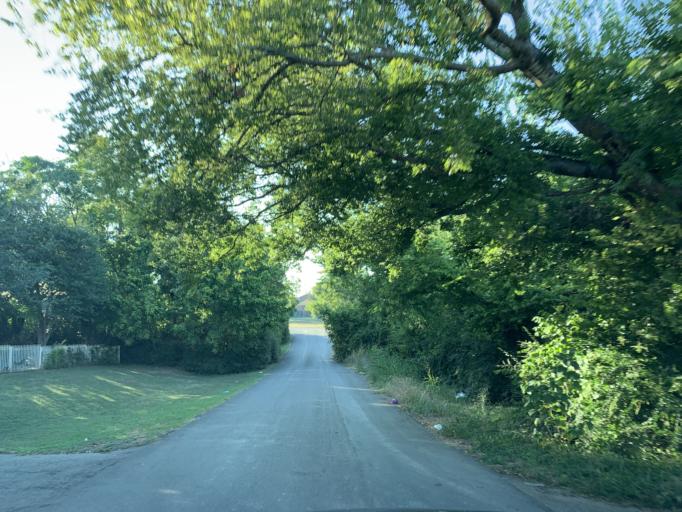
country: US
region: Texas
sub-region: Dallas County
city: Hutchins
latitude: 32.6682
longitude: -96.7810
